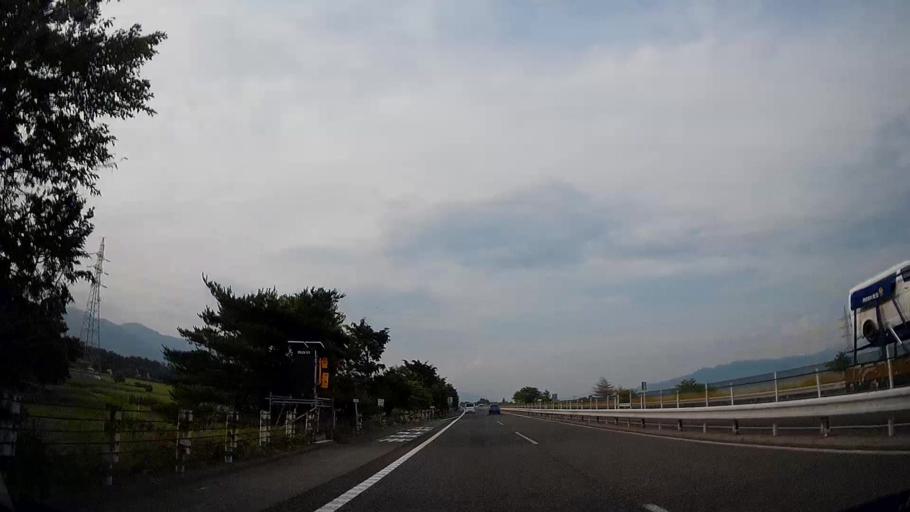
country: JP
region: Nagano
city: Ina
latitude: 35.8973
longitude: 137.9613
